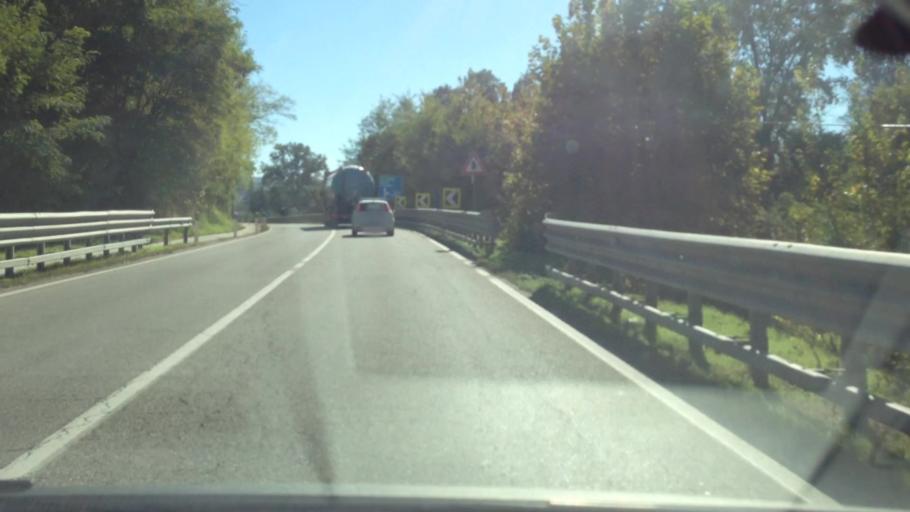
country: IT
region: Piedmont
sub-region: Provincia di Asti
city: Castello di Annone
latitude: 44.8850
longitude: 8.3104
